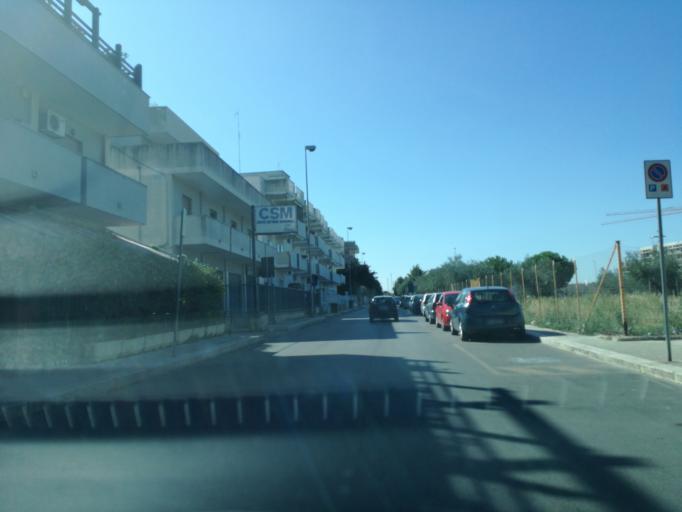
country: IT
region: Apulia
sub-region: Provincia di Bari
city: Capurso
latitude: 41.0498
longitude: 16.9154
